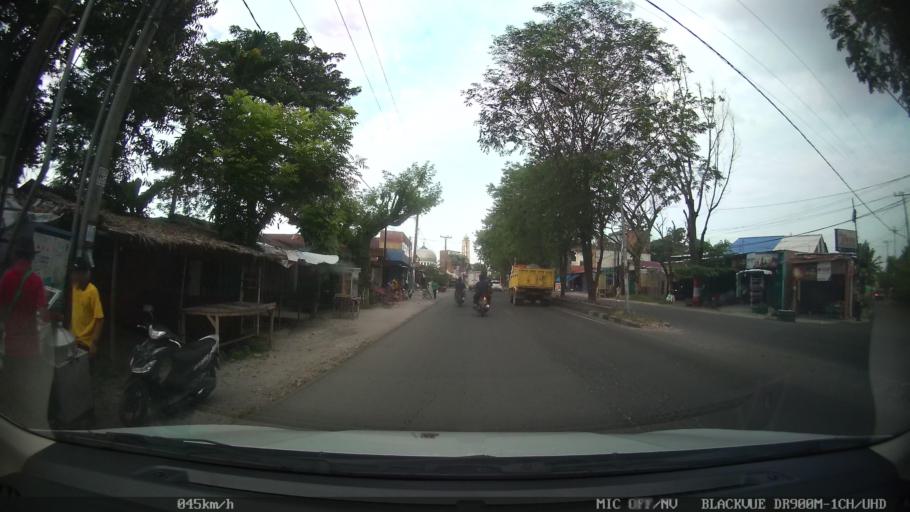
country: ID
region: North Sumatra
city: Sunggal
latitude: 3.5472
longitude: 98.6063
